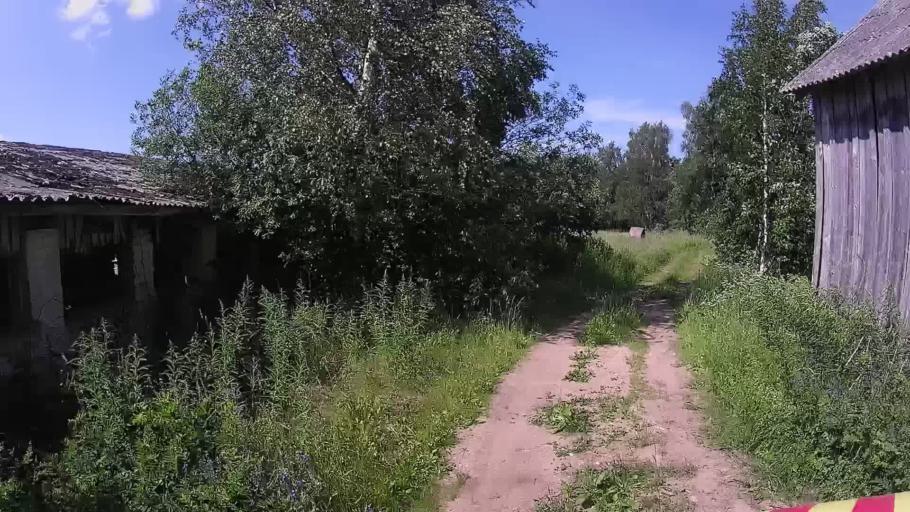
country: EE
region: Viljandimaa
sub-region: Karksi vald
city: Karksi-Nuia
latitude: 58.0050
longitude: 25.5134
